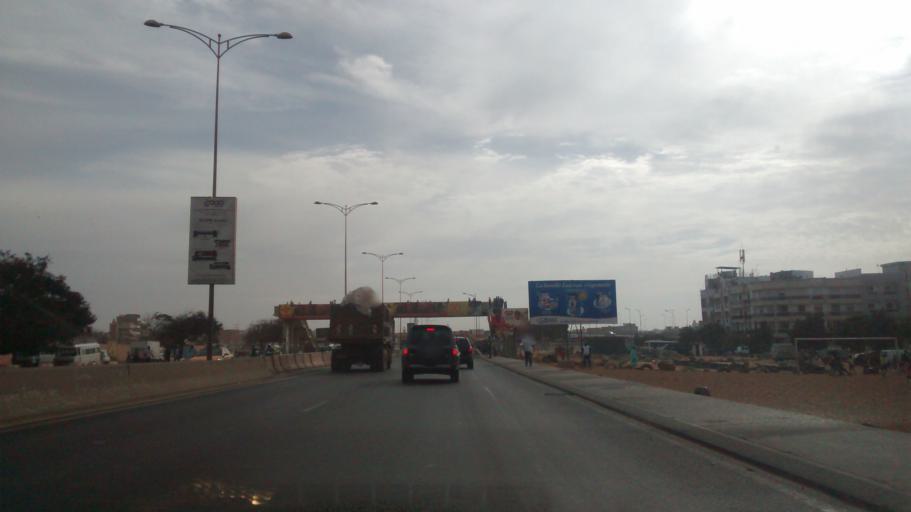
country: SN
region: Dakar
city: Grand Dakar
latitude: 14.7445
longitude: -17.4520
